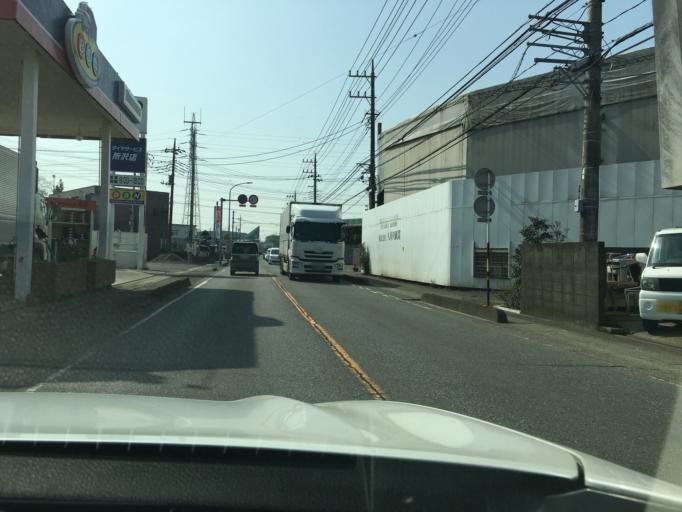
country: JP
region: Saitama
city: Tokorozawa
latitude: 35.8461
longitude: 139.4670
